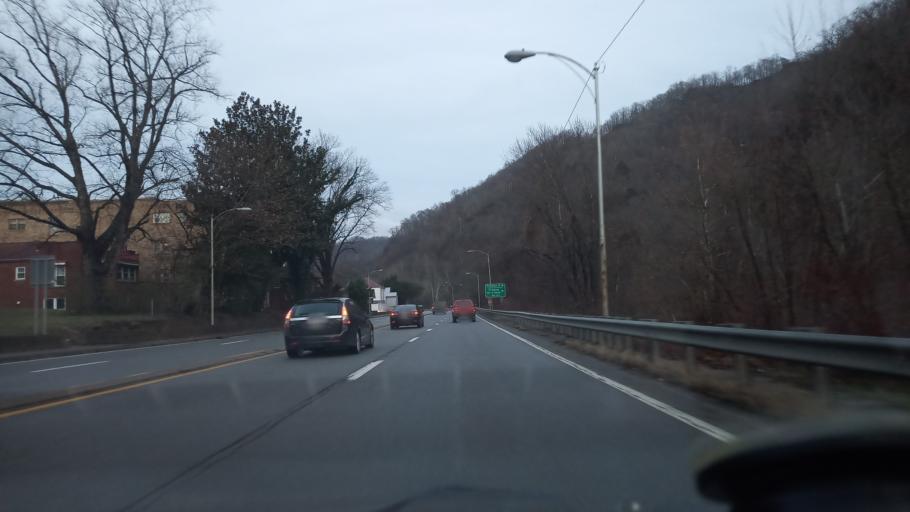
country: US
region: West Virginia
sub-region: Logan County
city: Logan
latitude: 37.8437
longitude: -81.9838
